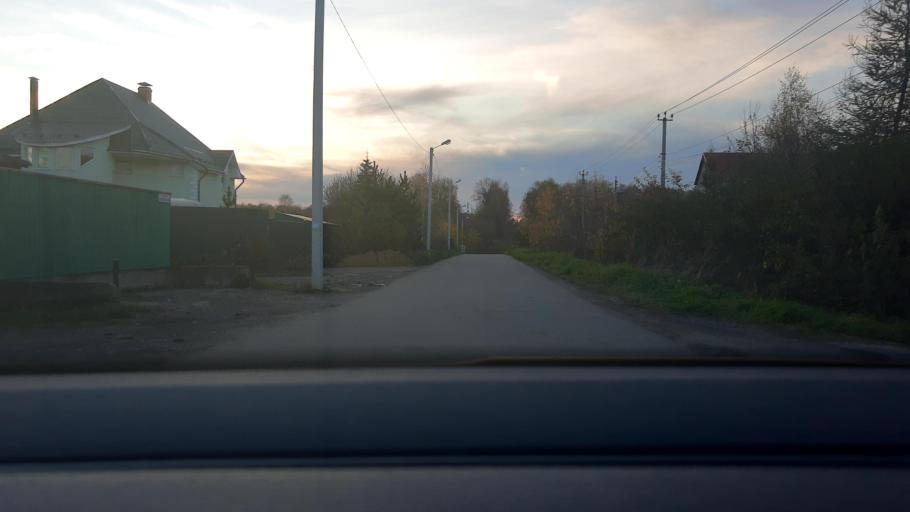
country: RU
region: Moskovskaya
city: Sheremet'yevskiy
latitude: 56.0036
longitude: 37.5224
